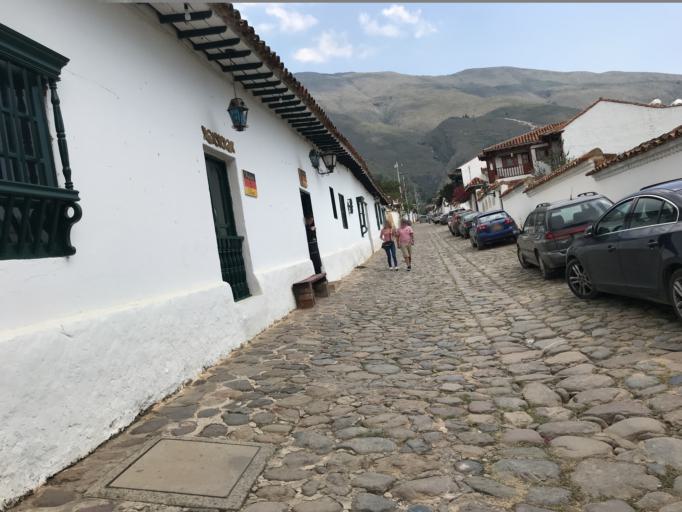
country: CO
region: Boyaca
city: Villa de Leiva
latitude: 5.6343
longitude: -73.5220
